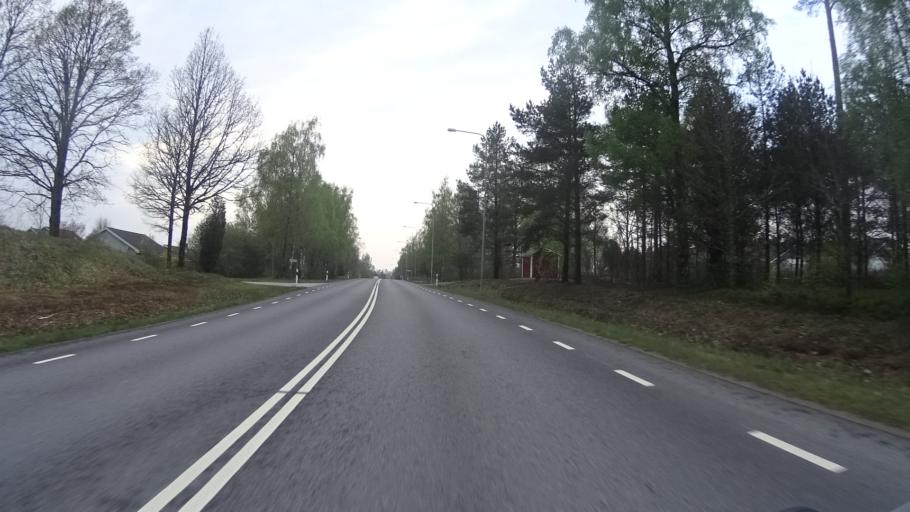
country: SE
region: Kronoberg
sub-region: Ljungby Kommun
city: Ljungby
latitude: 56.8323
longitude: 13.9745
